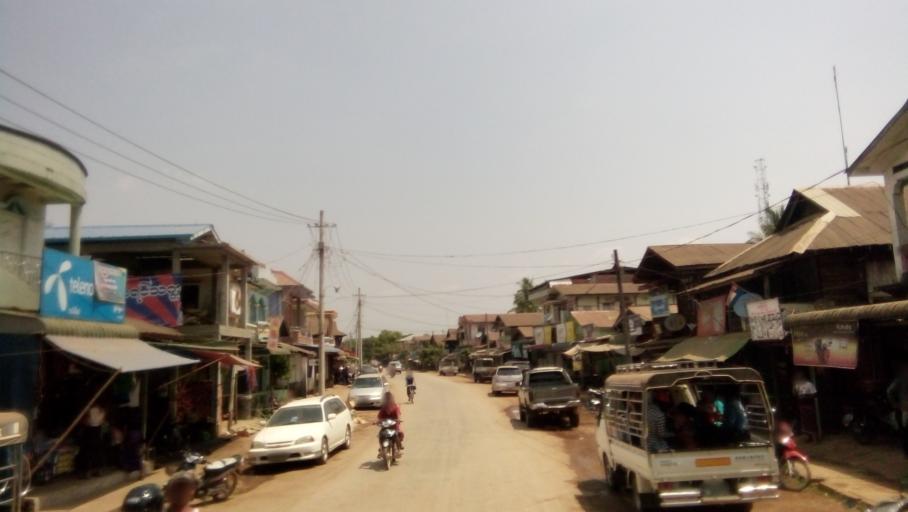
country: MM
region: Kayin
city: Hpa-an
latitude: 17.1212
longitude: 97.8191
